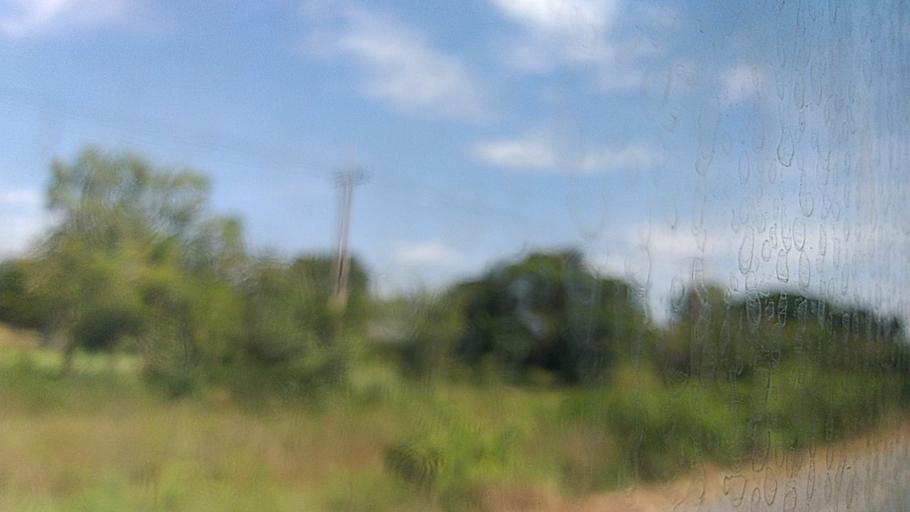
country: TH
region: Khon Kaen
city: Khon Kaen
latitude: 16.4045
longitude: 102.8817
